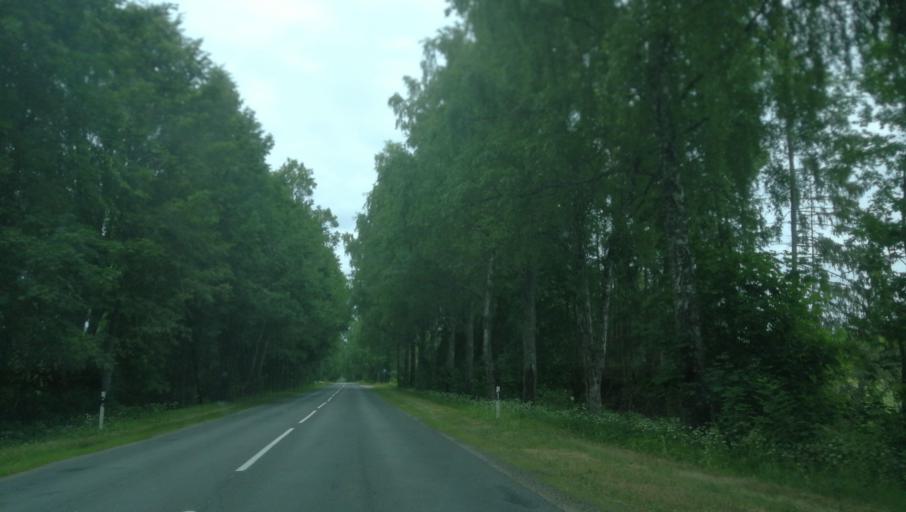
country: LV
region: Valmieras Rajons
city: Valmiera
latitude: 57.6745
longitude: 25.4302
